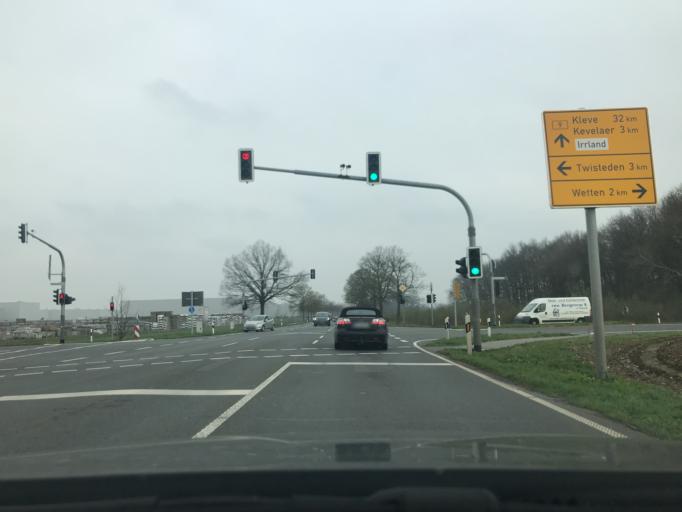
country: DE
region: North Rhine-Westphalia
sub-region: Regierungsbezirk Dusseldorf
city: Kevelaer
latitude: 51.5610
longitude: 6.2648
